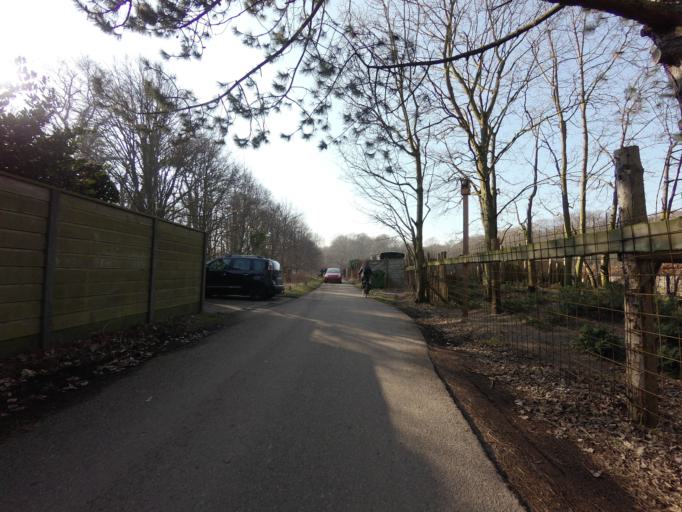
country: NL
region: North Holland
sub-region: Gemeente Bloemendaal
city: Bloemendaal
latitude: 52.4310
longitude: 4.6264
